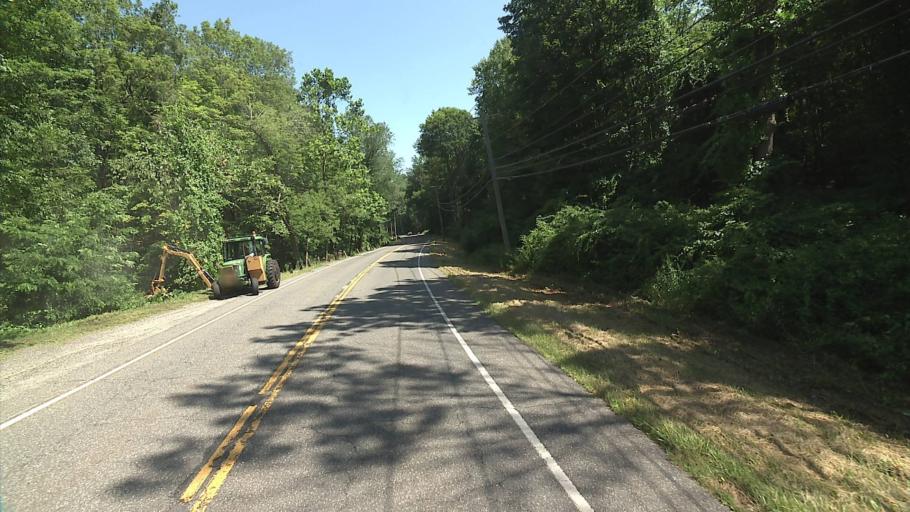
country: US
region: Connecticut
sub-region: Litchfield County
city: New Preston
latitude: 41.7040
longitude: -73.3456
